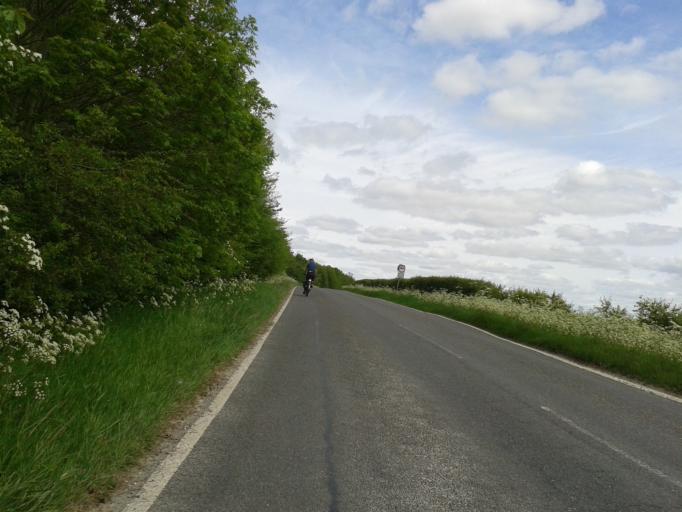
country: GB
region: England
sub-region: Cambridgeshire
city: Haslingfield
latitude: 52.1417
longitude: 0.0452
